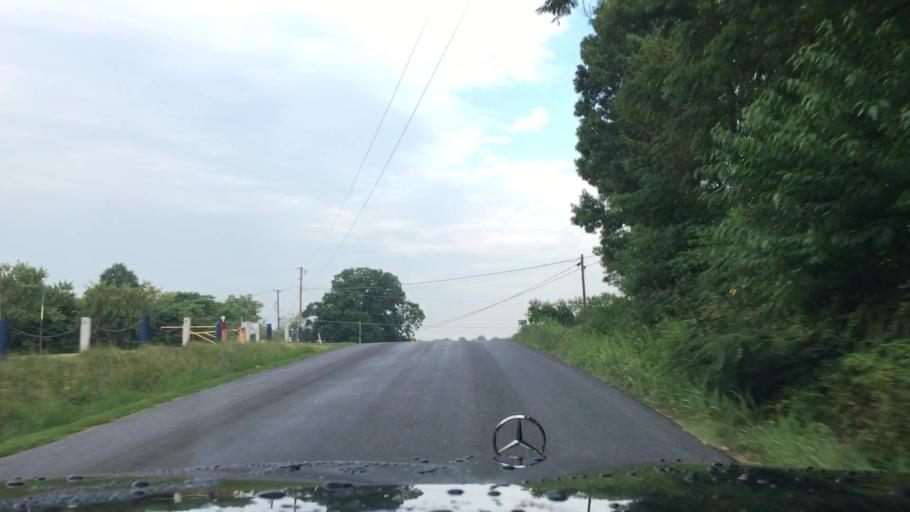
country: US
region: Virginia
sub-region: Campbell County
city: Altavista
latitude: 37.1480
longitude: -79.2947
